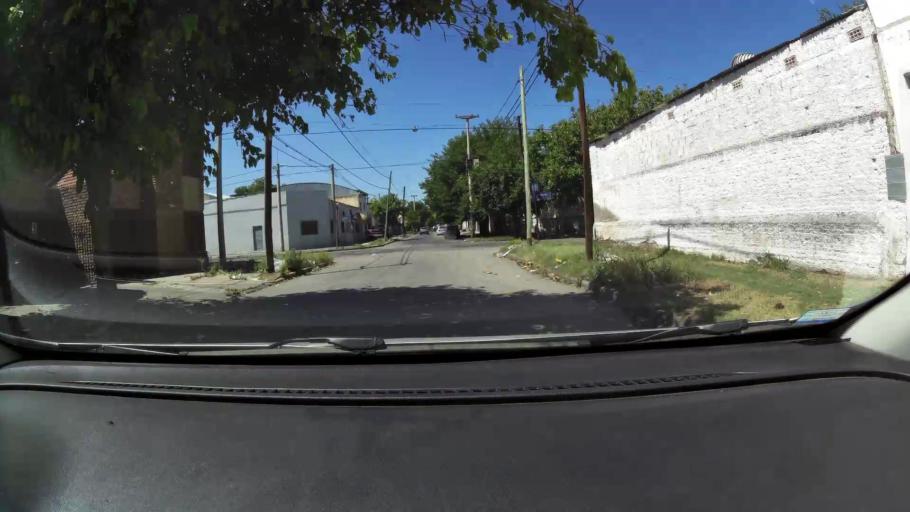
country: AR
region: Cordoba
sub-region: Departamento de Capital
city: Cordoba
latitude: -31.4200
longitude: -64.1476
